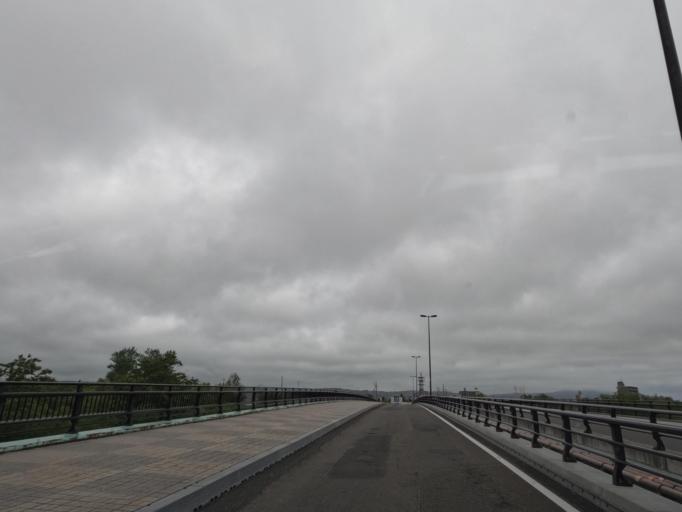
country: JP
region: Hokkaido
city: Tobetsu
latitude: 43.2128
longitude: 141.5178
